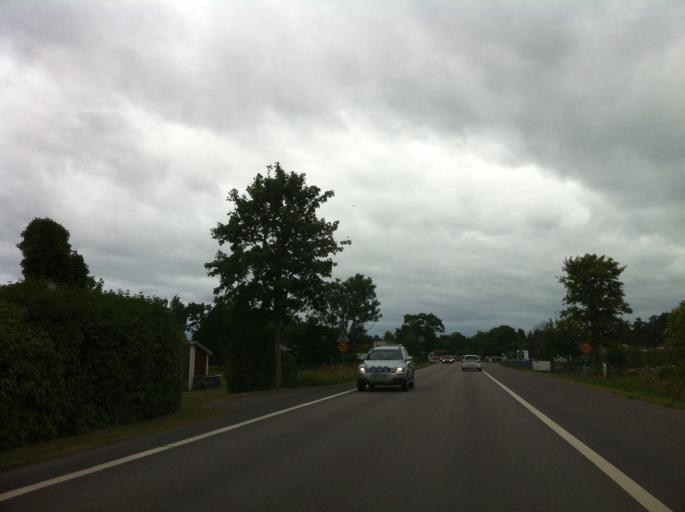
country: SE
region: Kalmar
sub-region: Borgholms Kommun
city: Borgholm
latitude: 57.2462
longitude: 17.0585
